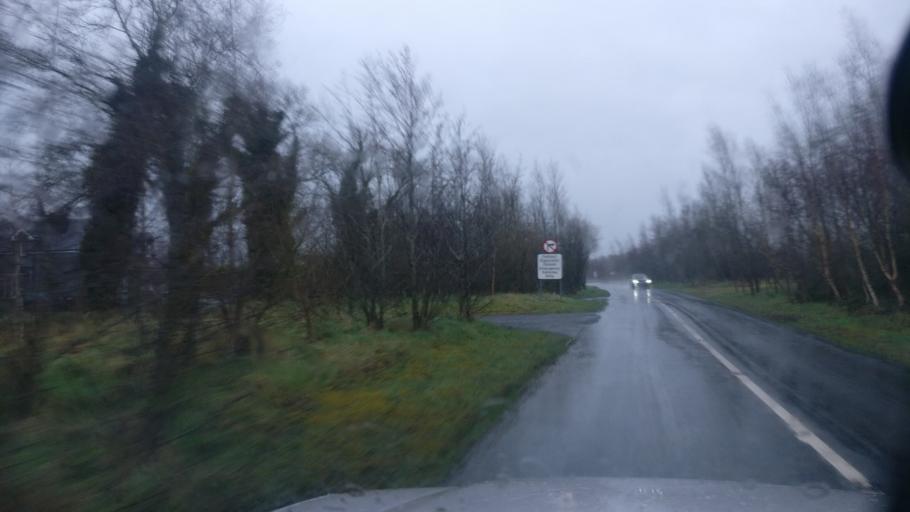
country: IE
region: Connaught
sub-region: County Galway
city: Ballinasloe
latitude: 53.3066
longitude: -8.3340
